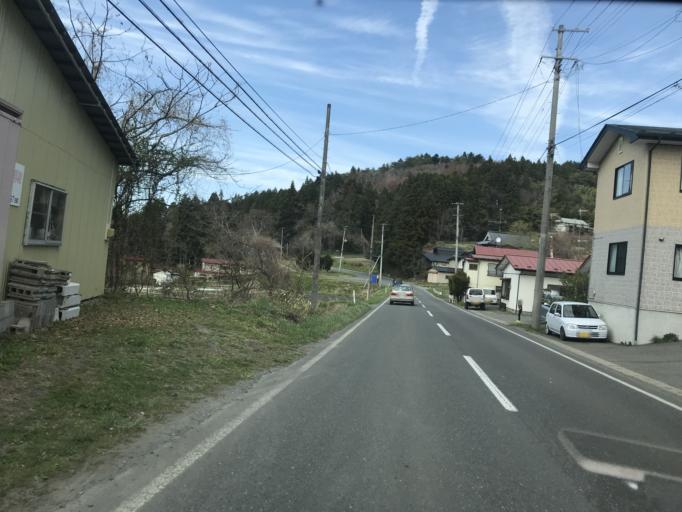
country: JP
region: Iwate
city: Ichinoseki
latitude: 38.8508
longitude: 141.3489
